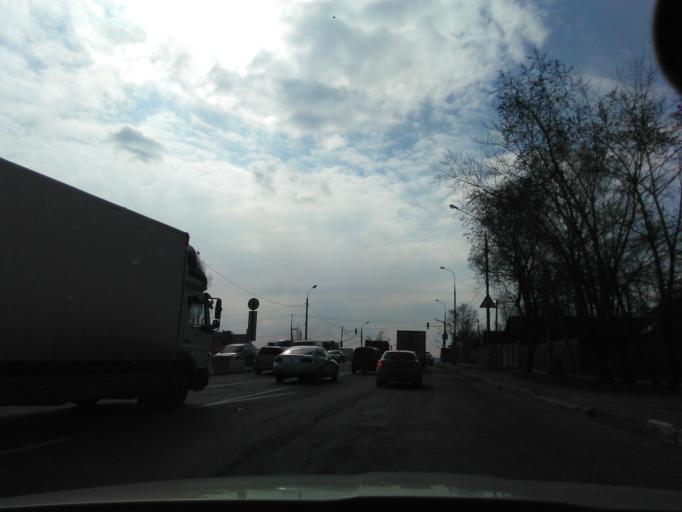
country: RU
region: Moscow
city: Severnyy
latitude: 55.9563
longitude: 37.5349
